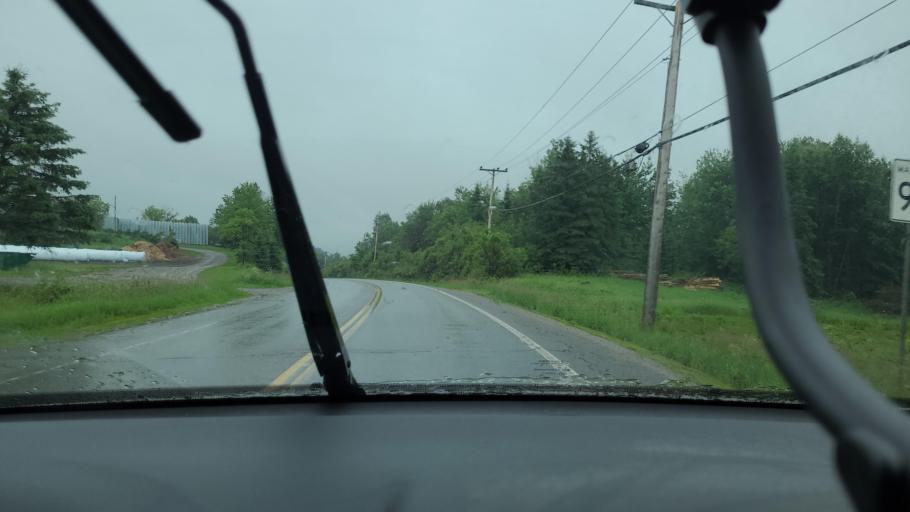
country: CA
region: Quebec
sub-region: Outaouais
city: Saint-Andre-Avellin
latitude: 45.6737
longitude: -75.0353
